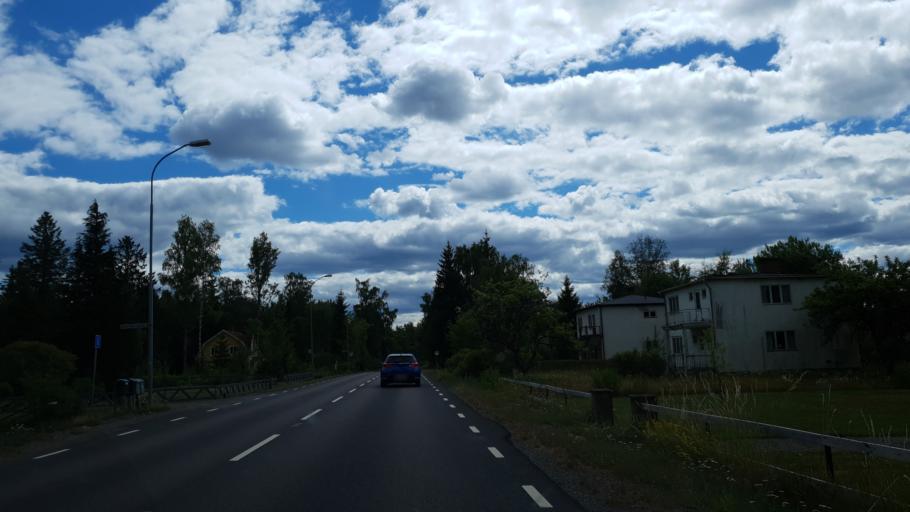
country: SE
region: Kalmar
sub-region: Emmaboda Kommun
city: Emmaboda
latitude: 56.9199
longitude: 15.5715
